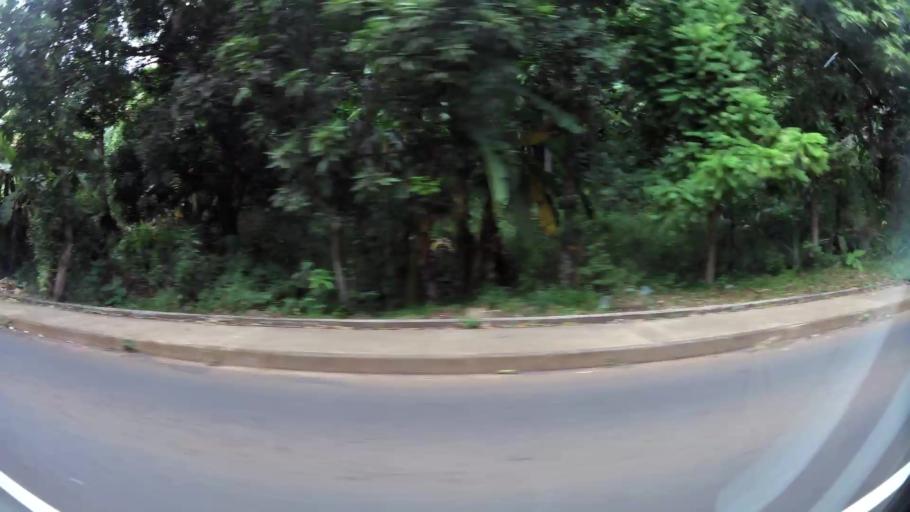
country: YT
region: Chiconi
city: Chiconi
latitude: -12.8411
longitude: 45.1200
